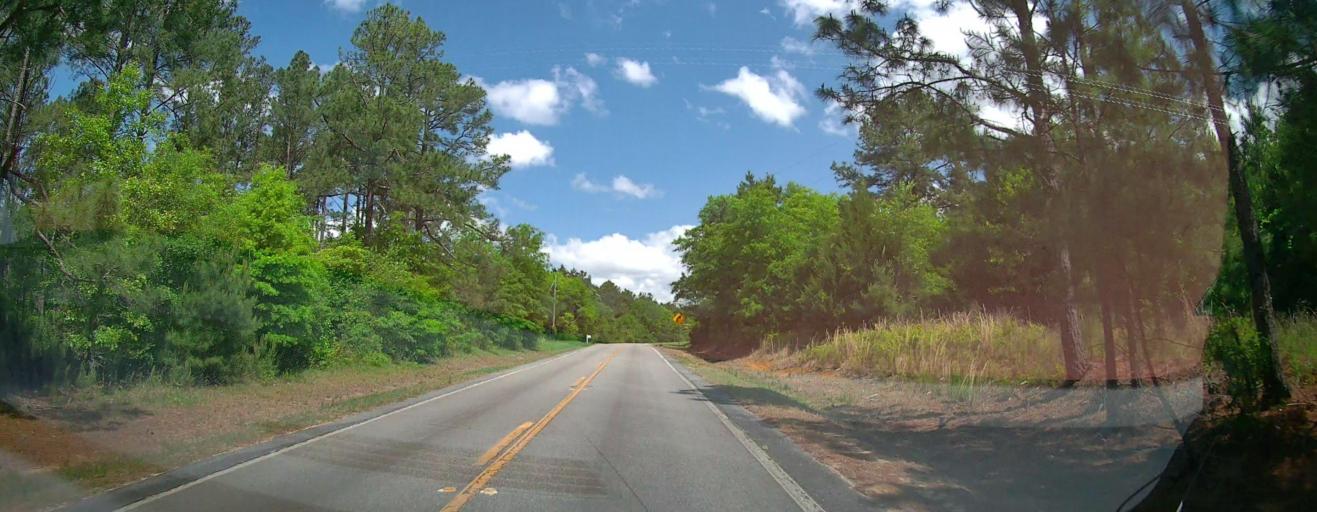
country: US
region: Georgia
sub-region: Bleckley County
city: Cochran
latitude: 32.4561
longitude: -83.2865
